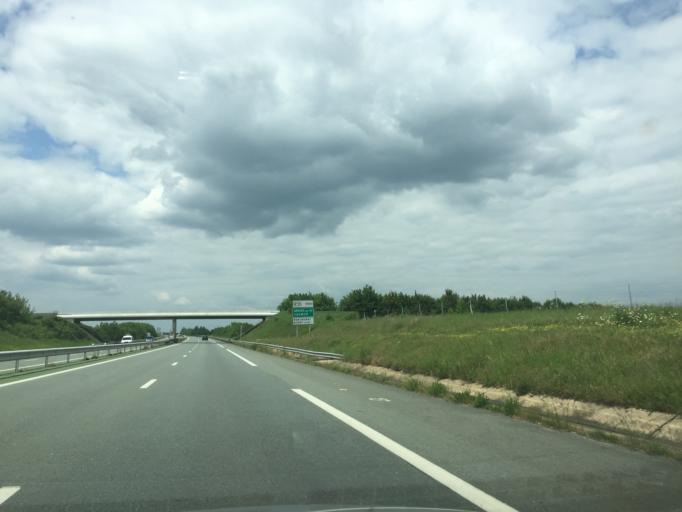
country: FR
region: Poitou-Charentes
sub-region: Departement des Deux-Sevres
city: Saint-Gelais
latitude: 46.4046
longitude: -0.3847
